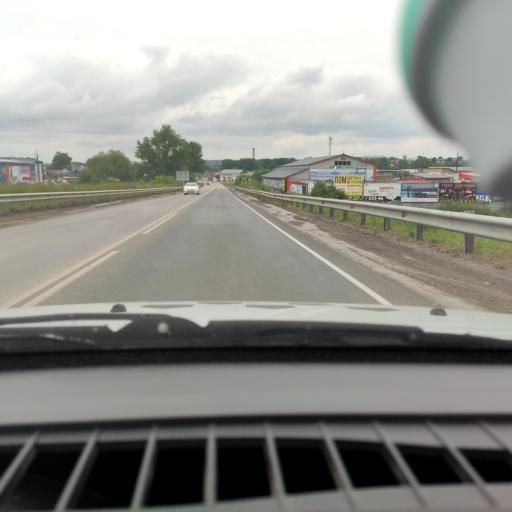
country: RU
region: Perm
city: Kungur
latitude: 57.4235
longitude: 56.9276
